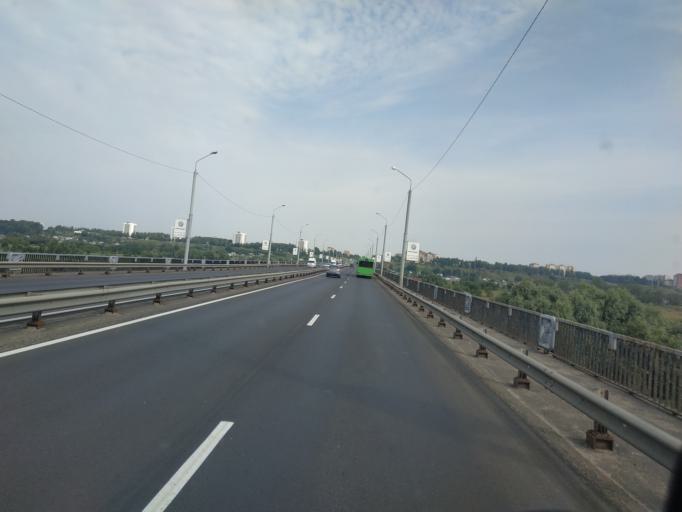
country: BY
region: Mogilev
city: Mahilyow
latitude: 53.8903
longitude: 30.3760
